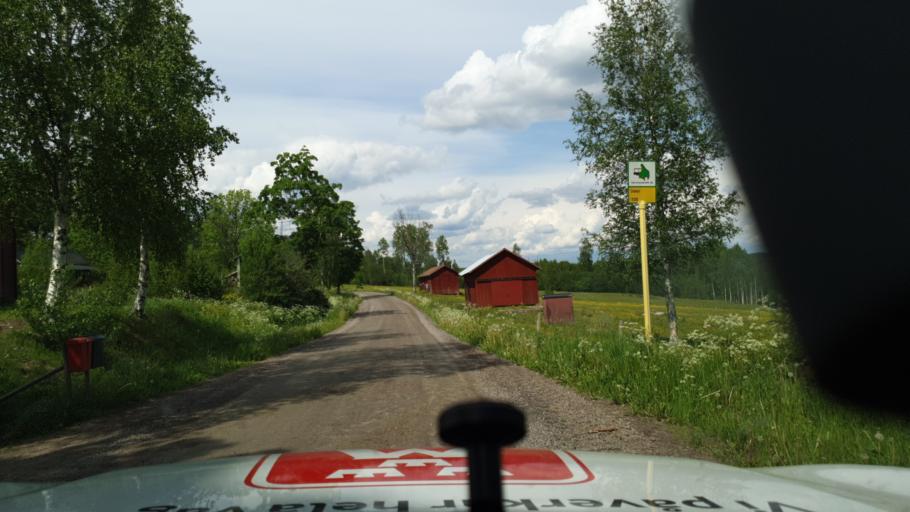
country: SE
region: Vaermland
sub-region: Torsby Kommun
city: Torsby
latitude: 59.9542
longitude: 12.8932
